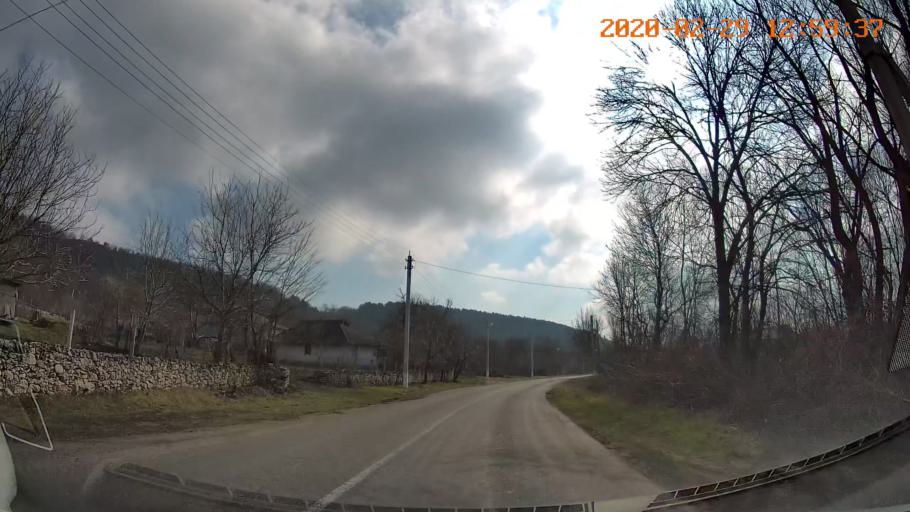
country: MD
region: Telenesti
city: Camenca
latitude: 48.0604
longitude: 28.7251
